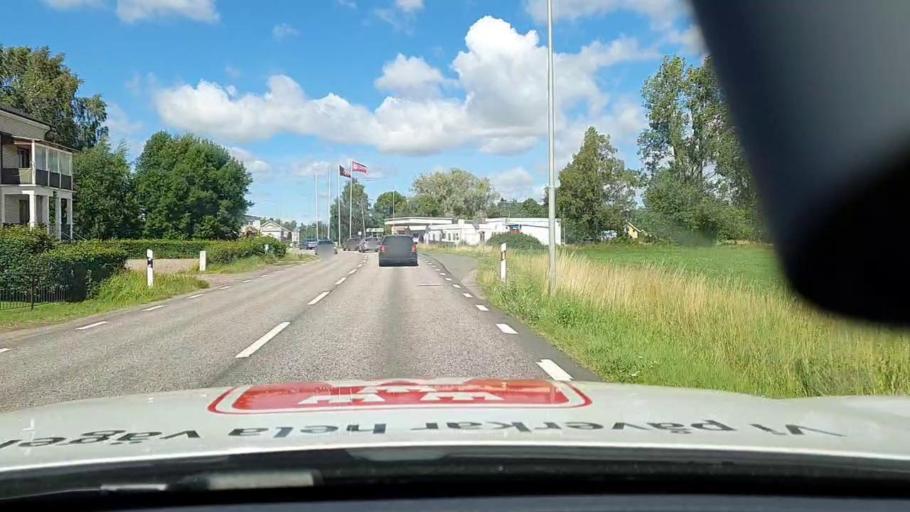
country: SE
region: Vaestra Goetaland
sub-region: Skovde Kommun
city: Stopen
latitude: 58.5679
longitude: 14.0100
